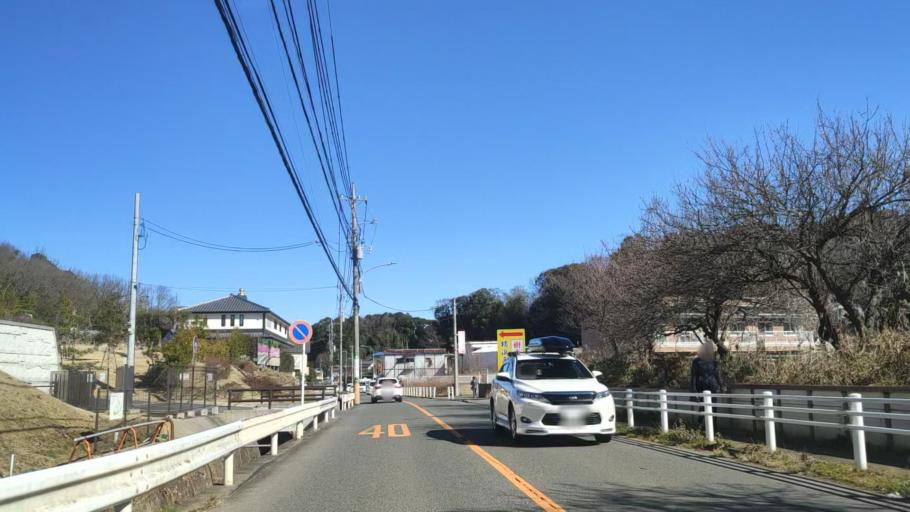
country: JP
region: Kanagawa
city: Minami-rinkan
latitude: 35.5078
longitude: 139.5189
